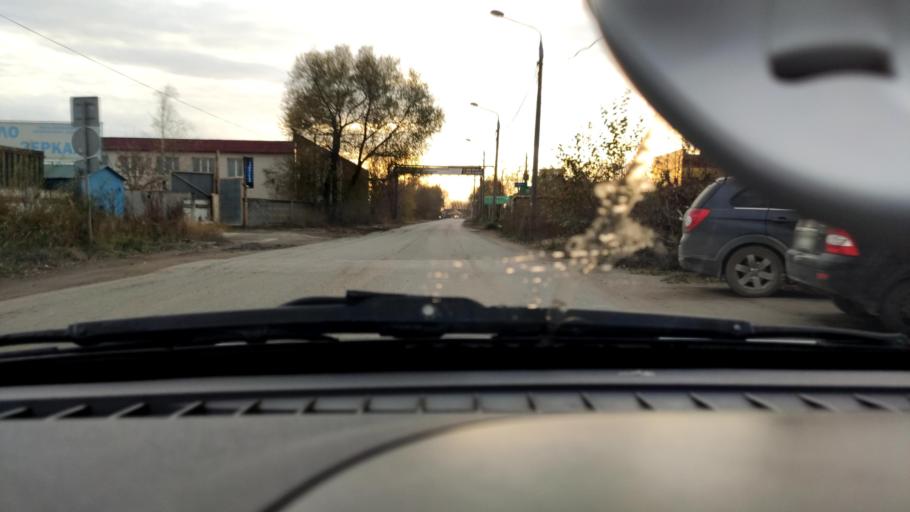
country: RU
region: Perm
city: Kondratovo
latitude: 58.0087
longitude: 56.0960
